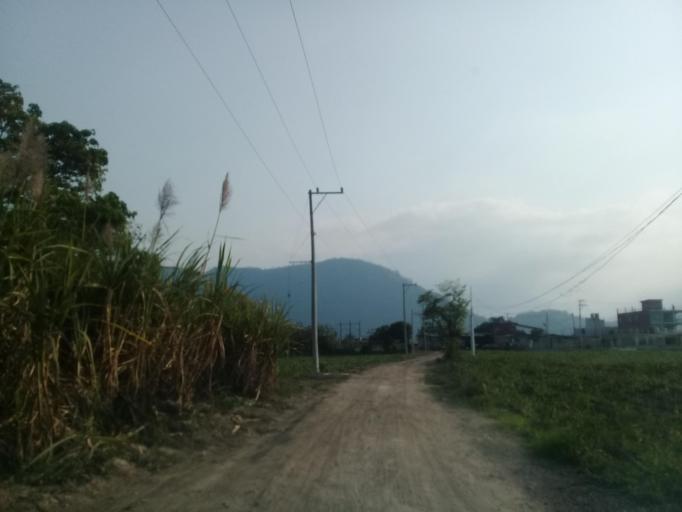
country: MX
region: Veracruz
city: Ixtac Zoquitlan
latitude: 18.8573
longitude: -97.0527
